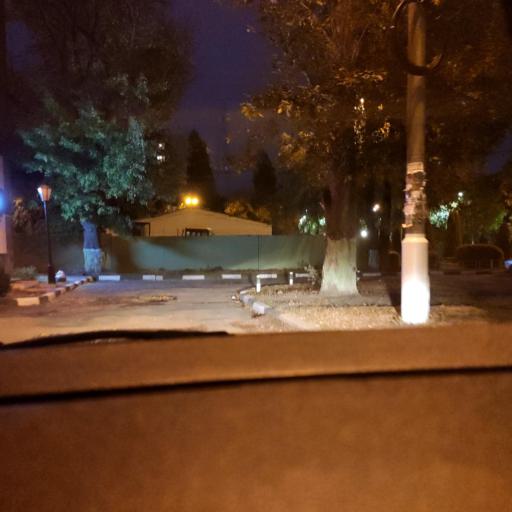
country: RU
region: Voronezj
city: Voronezh
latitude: 51.7027
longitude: 39.1721
